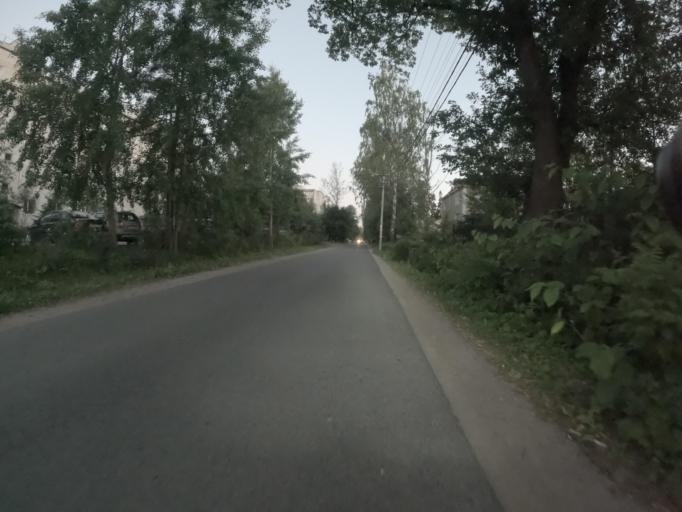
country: RU
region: Leningrad
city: Vsevolozhsk
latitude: 60.0148
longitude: 30.6152
